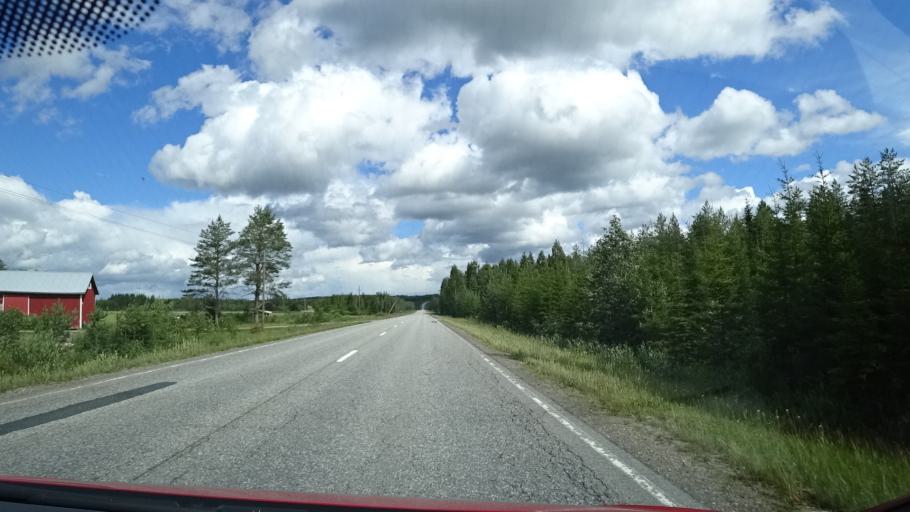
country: FI
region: Northern Savo
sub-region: Koillis-Savo
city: Rautavaara
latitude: 63.3267
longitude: 28.4292
